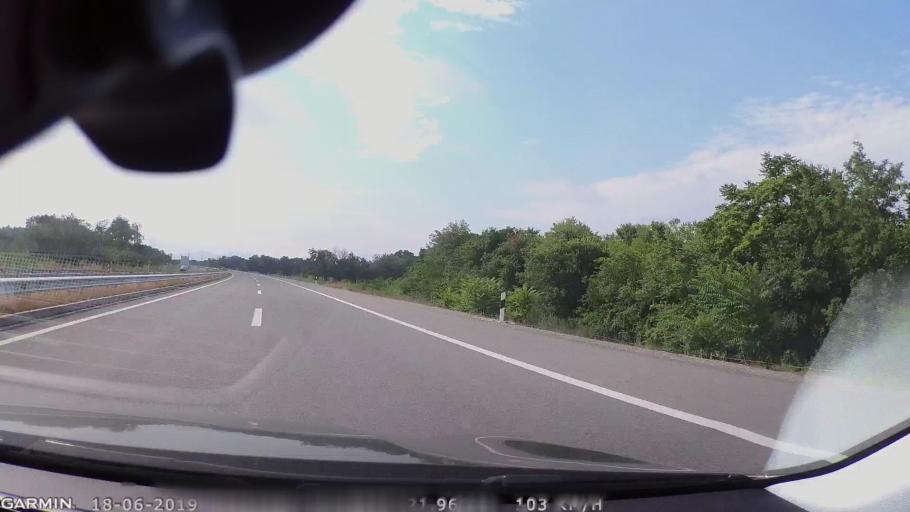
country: MK
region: Sveti Nikole
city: Sveti Nikole
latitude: 41.8507
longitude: 21.9643
